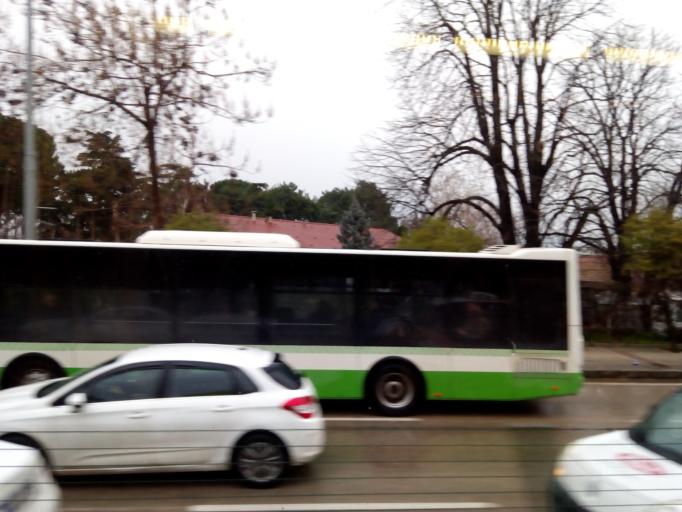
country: TR
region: Bursa
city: Yildirim
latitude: 40.2103
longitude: 29.0245
